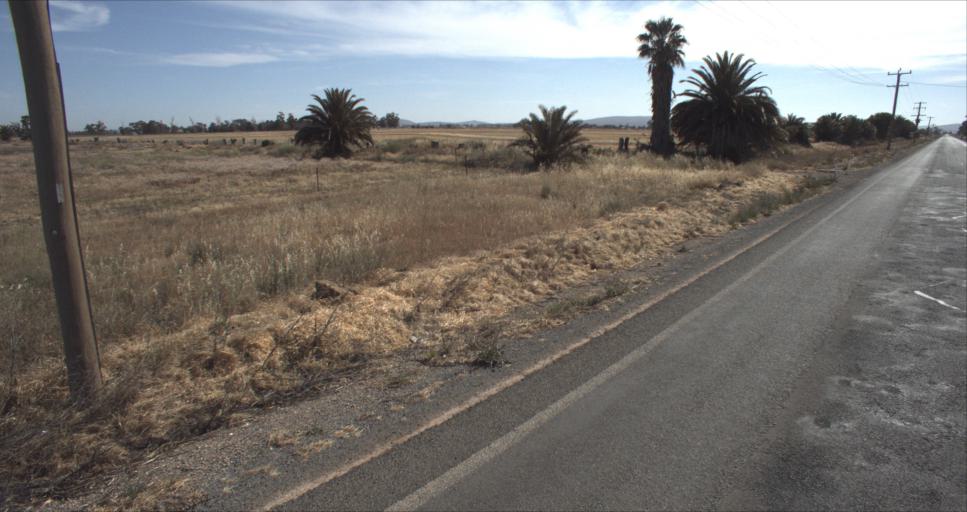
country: AU
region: New South Wales
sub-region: Leeton
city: Leeton
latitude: -34.5630
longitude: 146.4304
